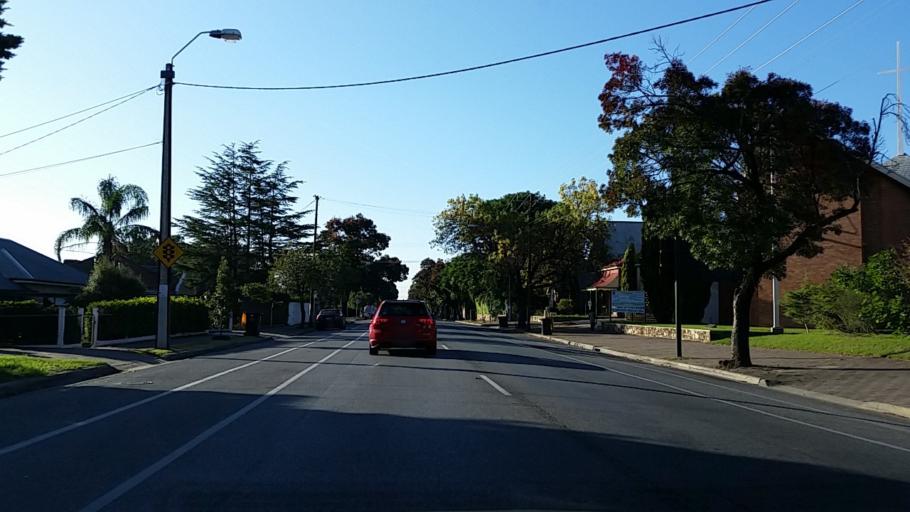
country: AU
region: South Australia
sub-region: Burnside
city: Hazelwood Park
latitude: -34.9363
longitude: 138.6600
